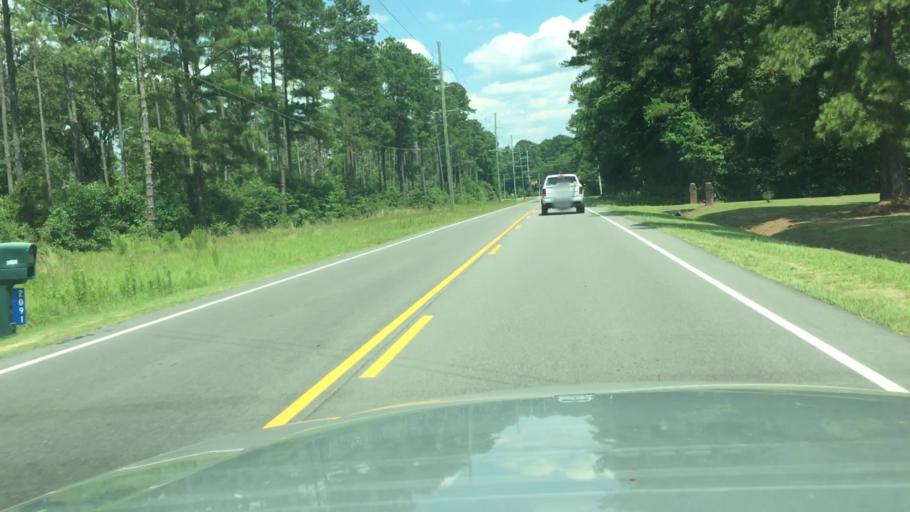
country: US
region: North Carolina
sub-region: Cumberland County
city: Vander
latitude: 34.9498
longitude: -78.8487
